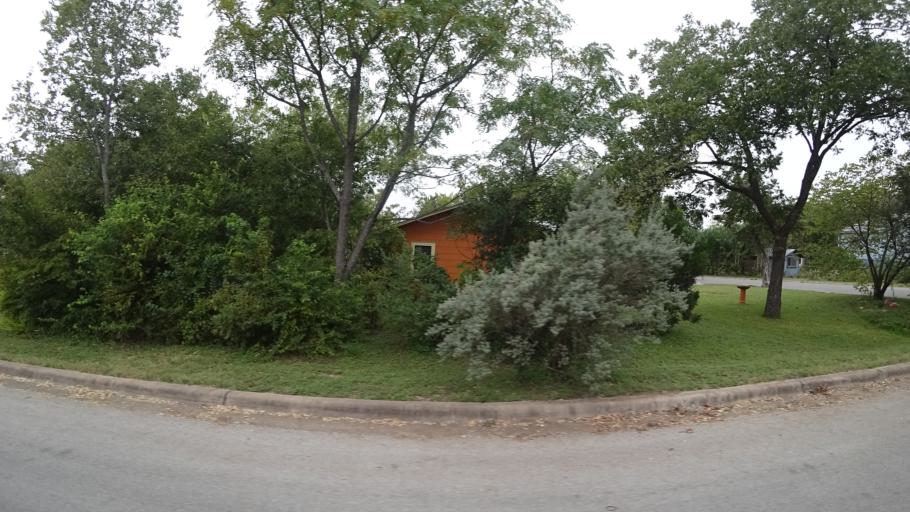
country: US
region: Texas
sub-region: Travis County
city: Austin
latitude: 30.2177
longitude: -97.7708
